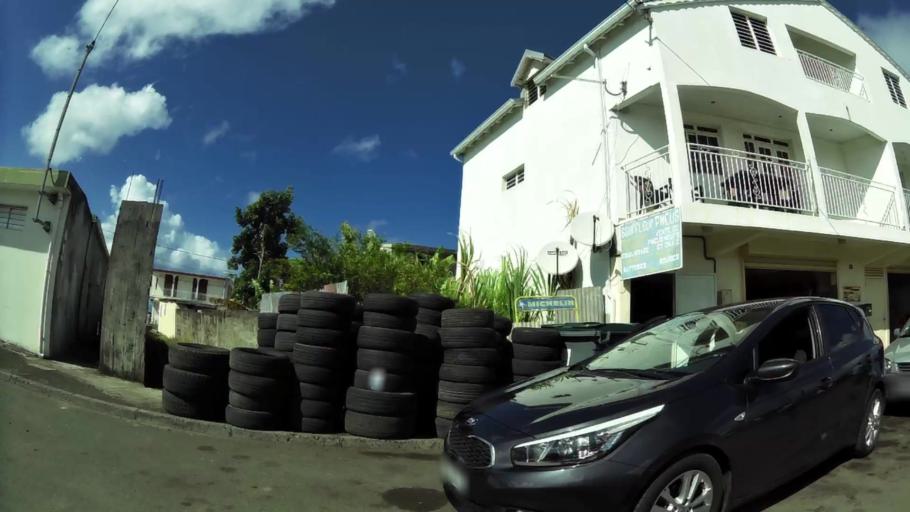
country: GP
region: Guadeloupe
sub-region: Guadeloupe
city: Port-Louis
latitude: 16.4204
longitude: -61.5333
